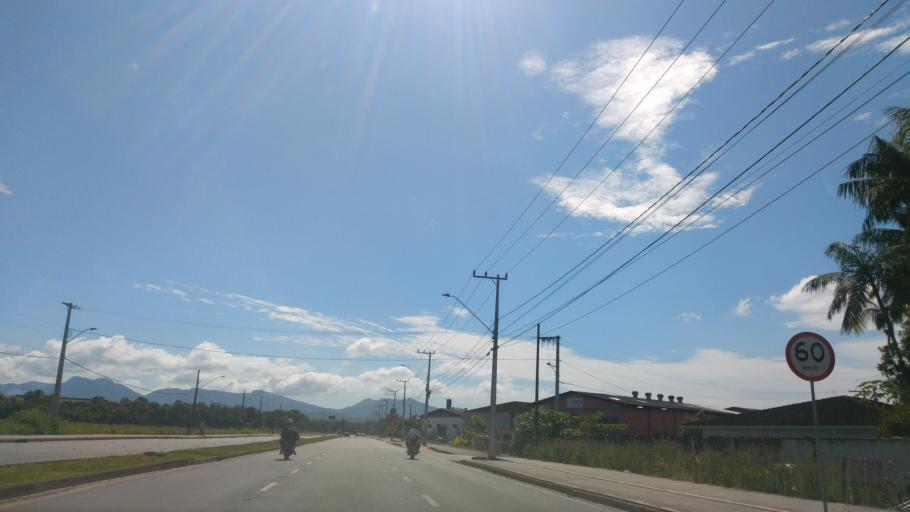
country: BR
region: Santa Catarina
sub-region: Joinville
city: Joinville
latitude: -26.2338
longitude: -48.8136
